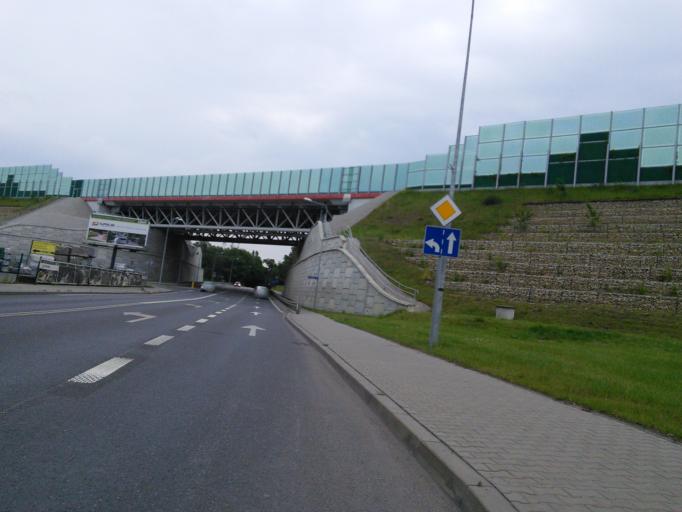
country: PL
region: Silesian Voivodeship
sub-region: Piekary Slaskie
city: Brzeziny Slaskie
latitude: 50.3711
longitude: 18.9586
